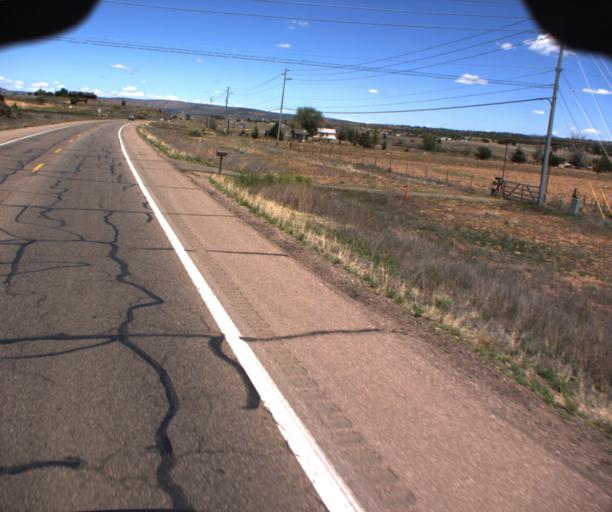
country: US
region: Arizona
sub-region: Yavapai County
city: Paulden
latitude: 34.8643
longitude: -112.4700
